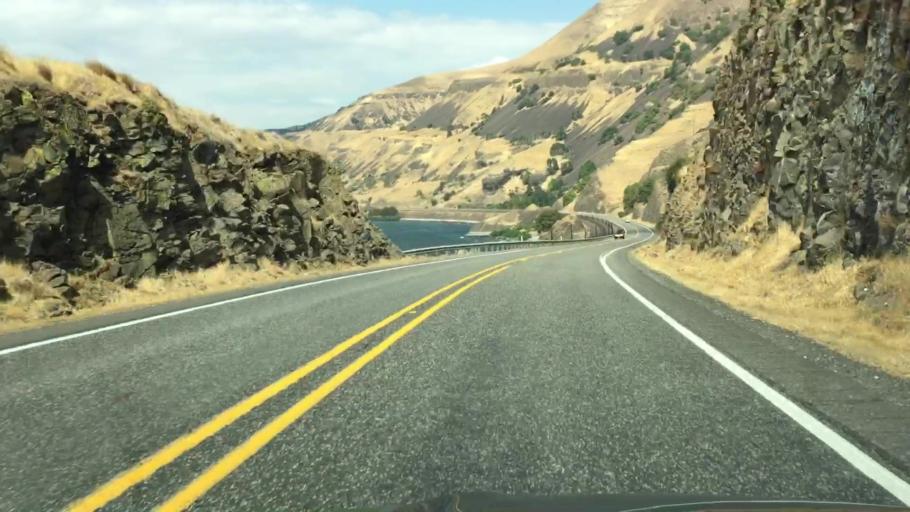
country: US
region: Oregon
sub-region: Wasco County
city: Chenoweth
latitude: 45.6686
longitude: -121.2070
